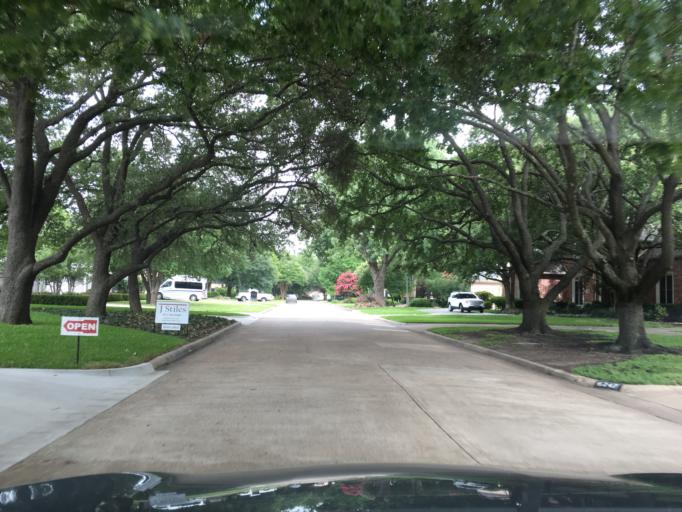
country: US
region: Texas
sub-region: Dallas County
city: University Park
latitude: 32.8812
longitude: -96.7977
